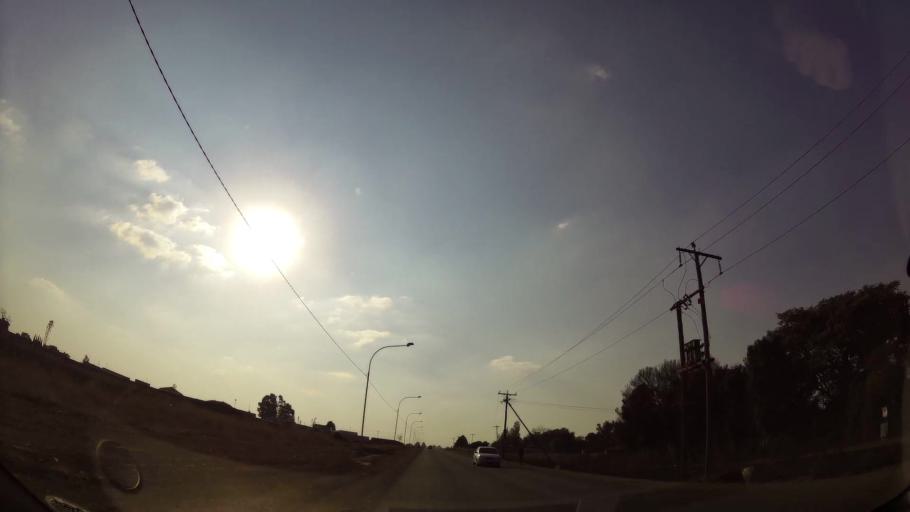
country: ZA
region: Gauteng
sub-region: Ekurhuleni Metropolitan Municipality
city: Benoni
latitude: -26.1053
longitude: 28.3846
